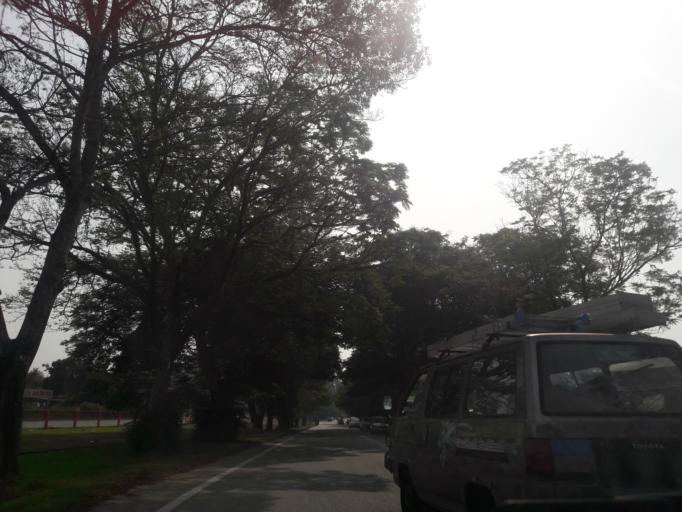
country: MY
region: Kedah
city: Kulim
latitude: 5.3484
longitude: 100.5236
